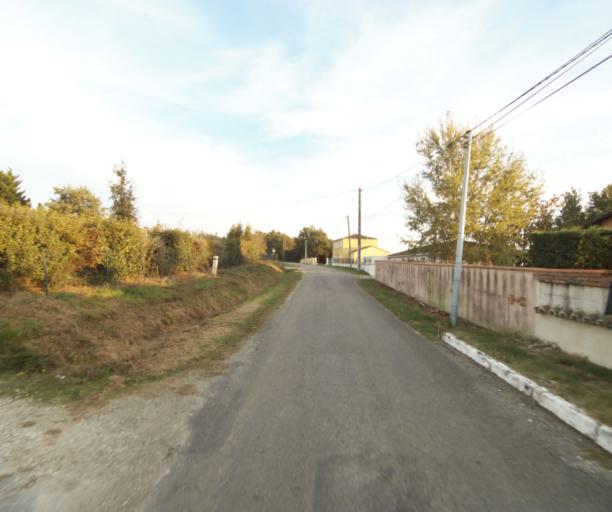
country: FR
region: Midi-Pyrenees
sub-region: Departement du Tarn-et-Garonne
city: Pompignan
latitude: 43.8286
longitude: 1.3105
